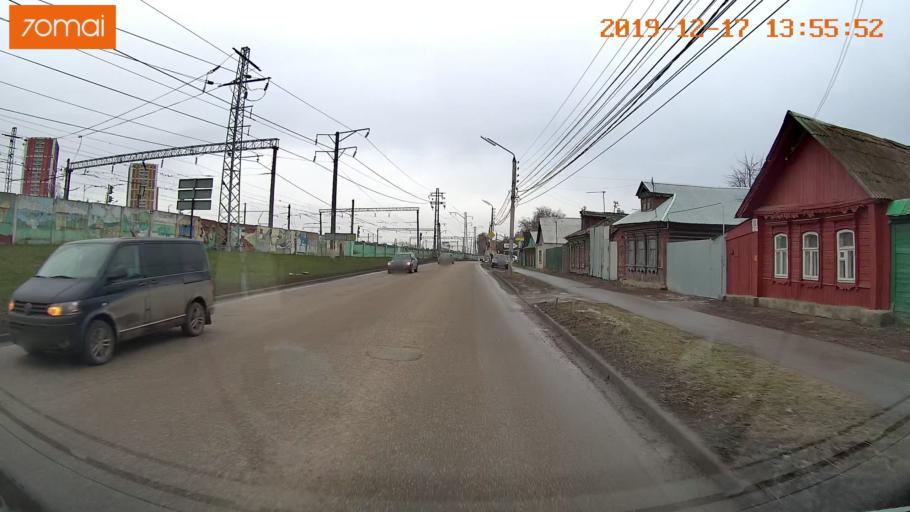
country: RU
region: Rjazan
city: Ryazan'
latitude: 54.6306
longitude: 39.7018
